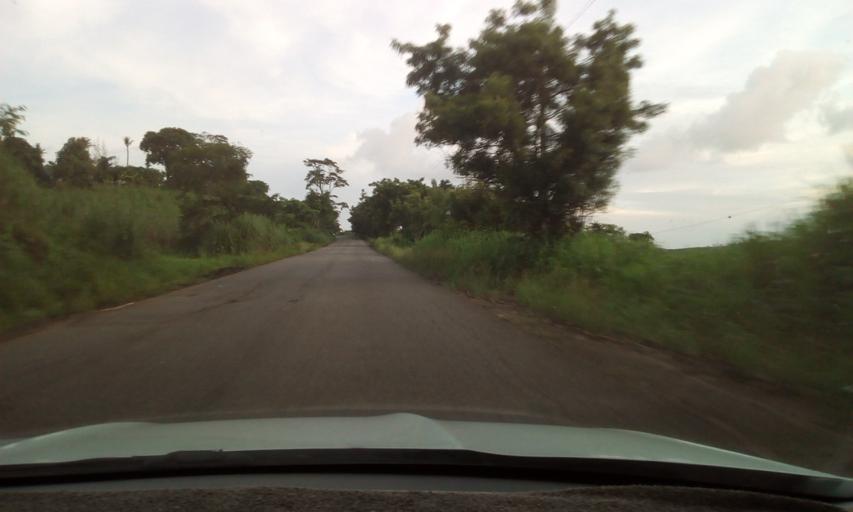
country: BR
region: Pernambuco
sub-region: Condado
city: Condado
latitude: -7.6004
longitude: -35.2130
